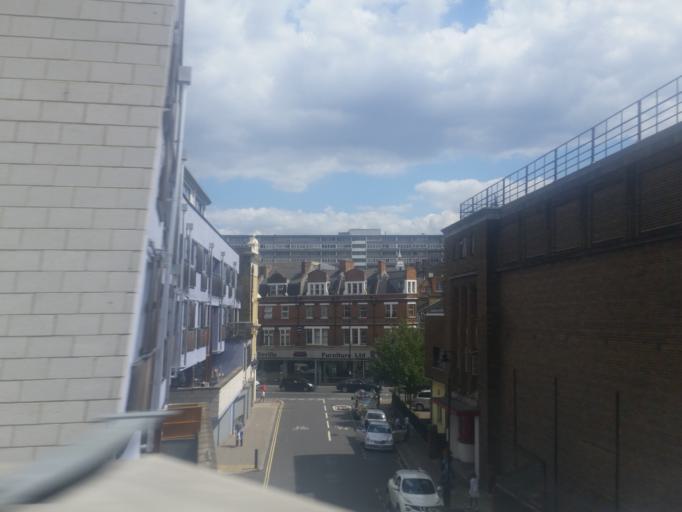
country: GB
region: England
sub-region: Greater London
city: Camberwell
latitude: 51.4832
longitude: -0.0956
